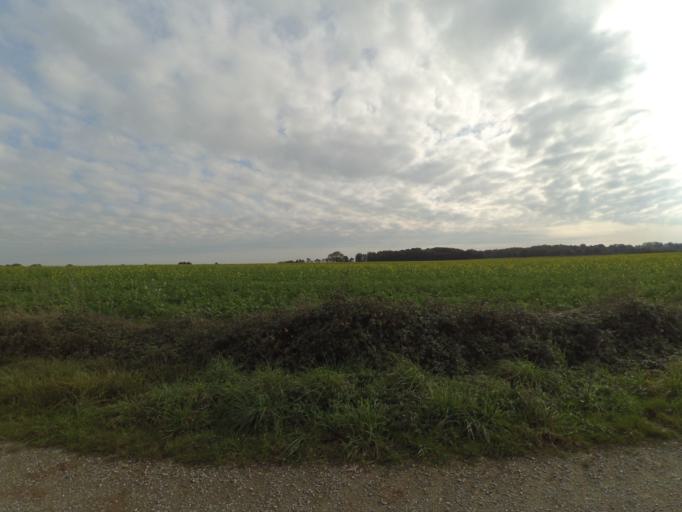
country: FR
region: Pays de la Loire
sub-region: Departement de la Loire-Atlantique
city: La Planche
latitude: 46.9952
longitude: -1.3895
